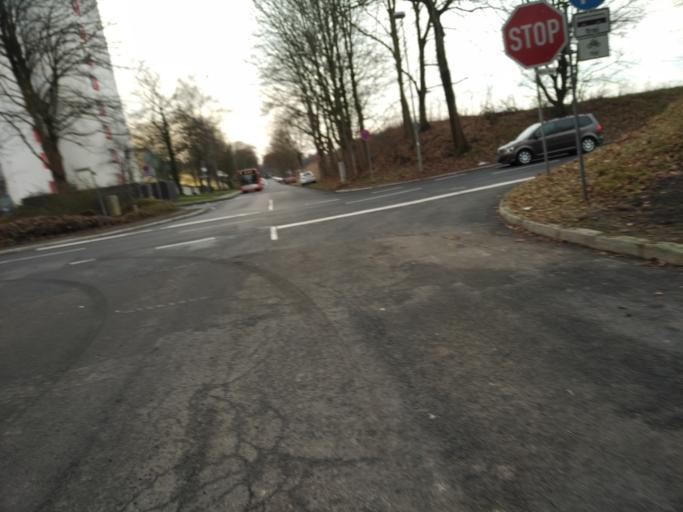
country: DE
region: North Rhine-Westphalia
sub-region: Regierungsbezirk Koln
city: Odenthal
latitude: 51.0510
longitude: 7.0762
